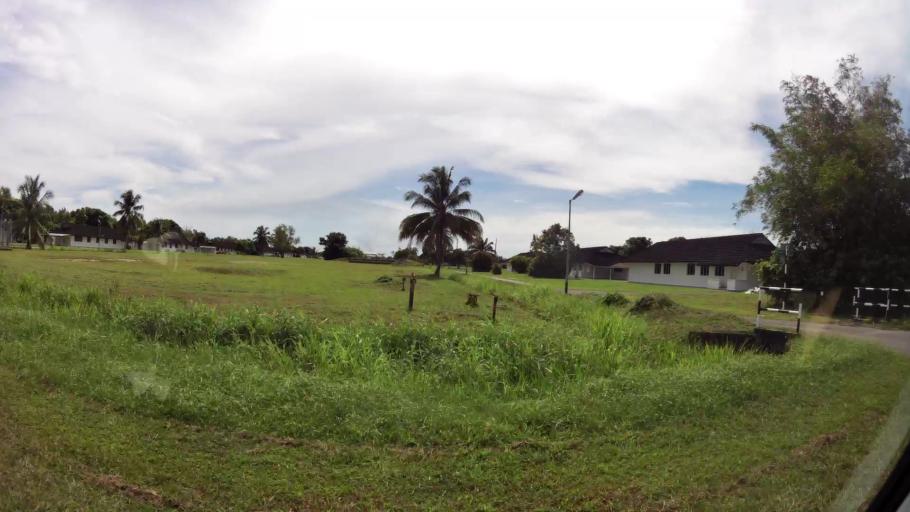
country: BN
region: Belait
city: Seria
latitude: 4.6108
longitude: 114.3192
